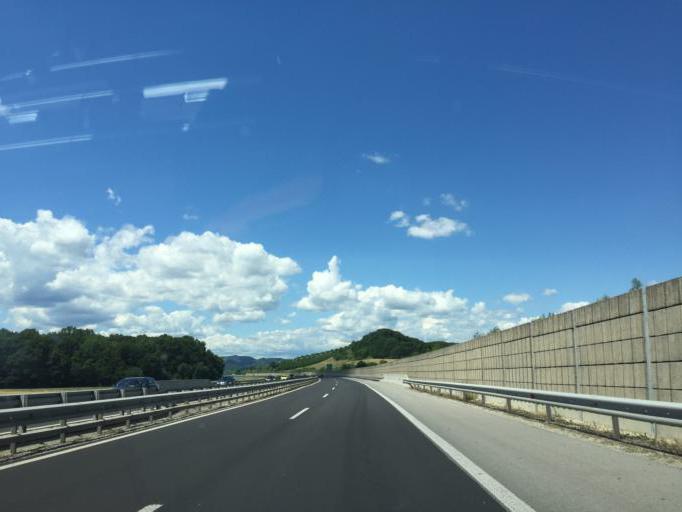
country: SI
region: Pesnica
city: Pesnica pri Mariboru
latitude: 46.5907
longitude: 15.7127
